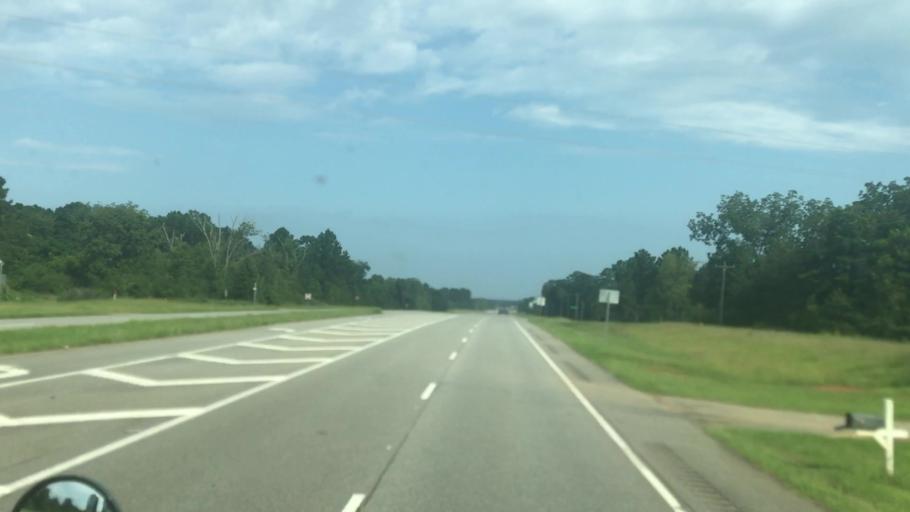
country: US
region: Georgia
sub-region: Early County
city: Blakely
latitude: 31.3442
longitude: -84.9094
